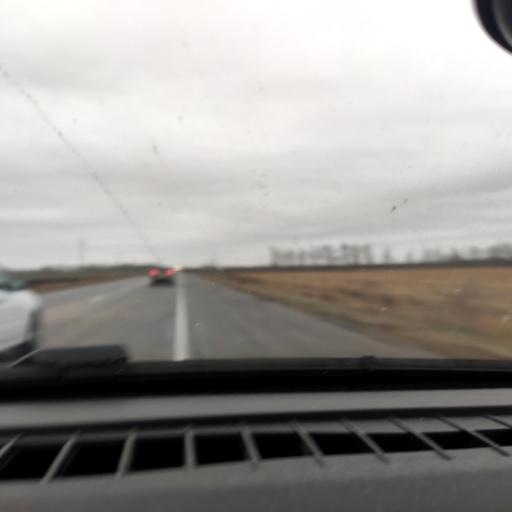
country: RU
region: Voronezj
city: Strelitsa
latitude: 51.5564
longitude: 38.9727
